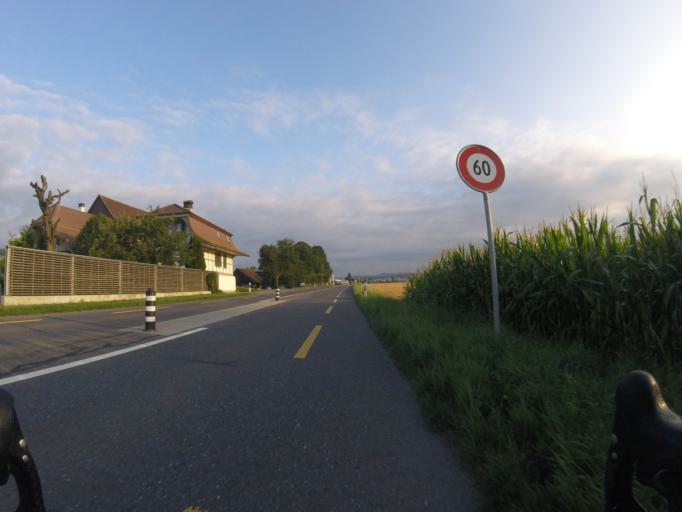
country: CH
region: Bern
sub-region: Bern-Mittelland District
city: Niederwichtrach
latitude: 46.8600
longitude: 7.5672
